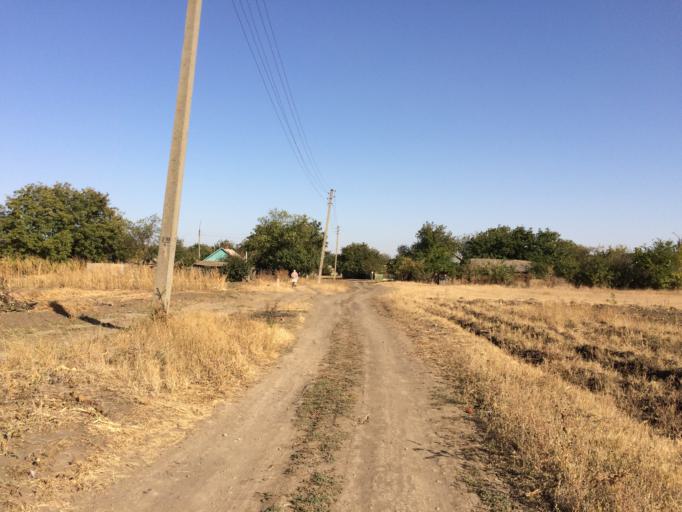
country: RU
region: Rostov
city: Tselina
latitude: 46.5216
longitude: 41.1866
